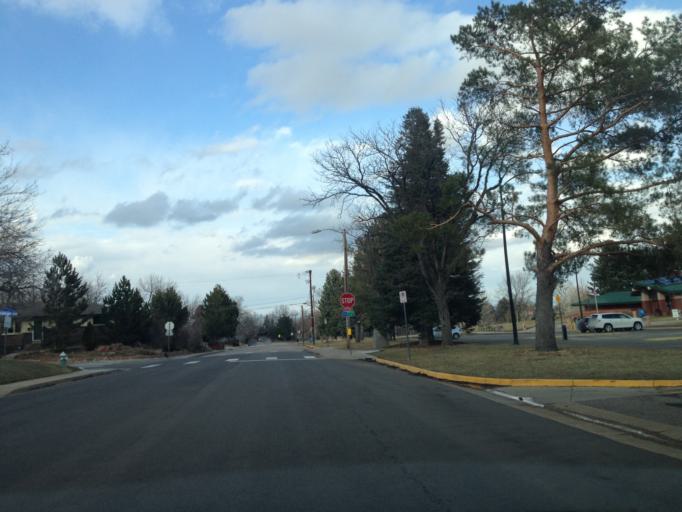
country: US
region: Colorado
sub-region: Boulder County
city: Boulder
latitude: 39.9744
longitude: -105.2501
